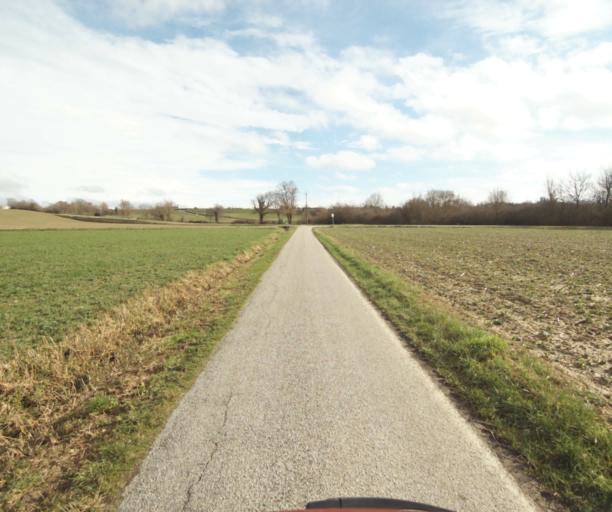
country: FR
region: Midi-Pyrenees
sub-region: Departement de l'Ariege
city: La Tour-du-Crieu
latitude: 43.1307
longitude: 1.7023
